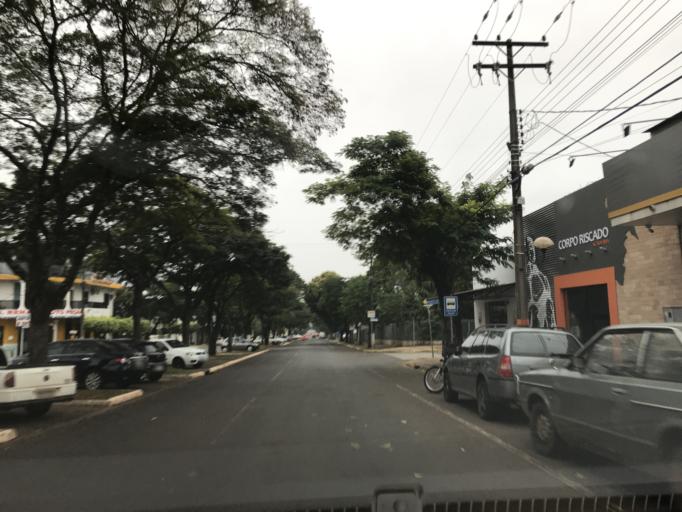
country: PY
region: Canindeyu
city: Salto del Guaira
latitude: -24.1605
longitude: -54.0986
